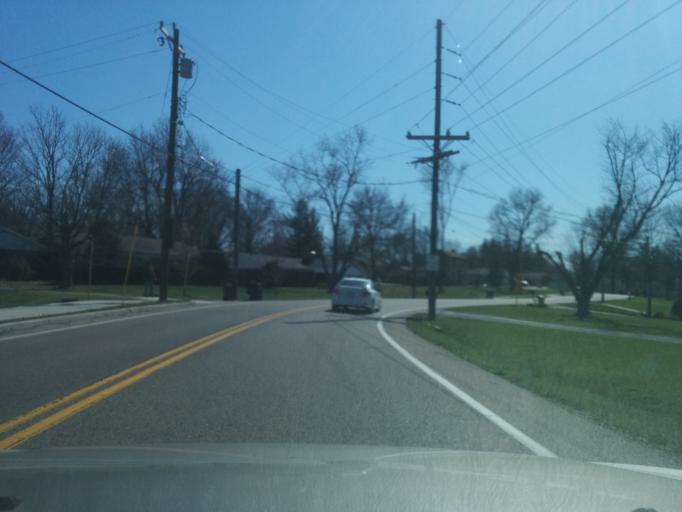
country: US
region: Ohio
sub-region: Hamilton County
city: Dry Ridge
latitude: 39.2381
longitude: -84.6137
